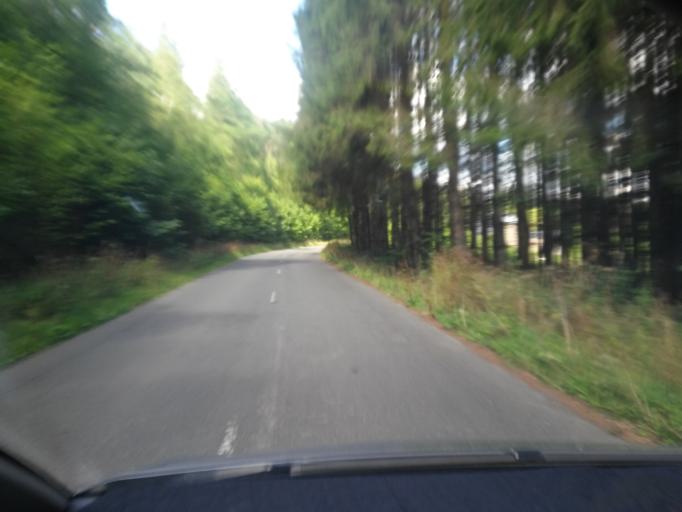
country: BE
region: Wallonia
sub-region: Province du Luxembourg
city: Libin
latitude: 50.0273
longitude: 5.3052
